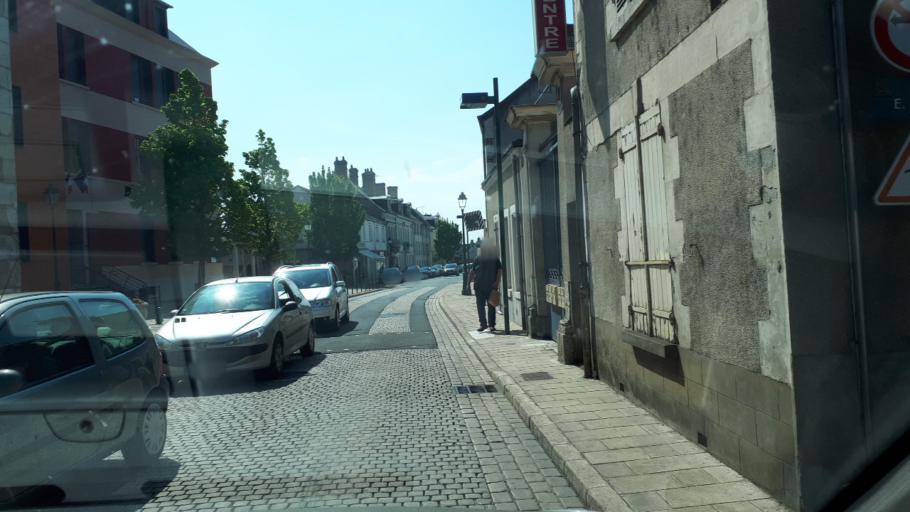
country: FR
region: Centre
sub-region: Departement du Loir-et-Cher
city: Romorantin-Lanthenay
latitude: 47.3632
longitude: 1.7421
